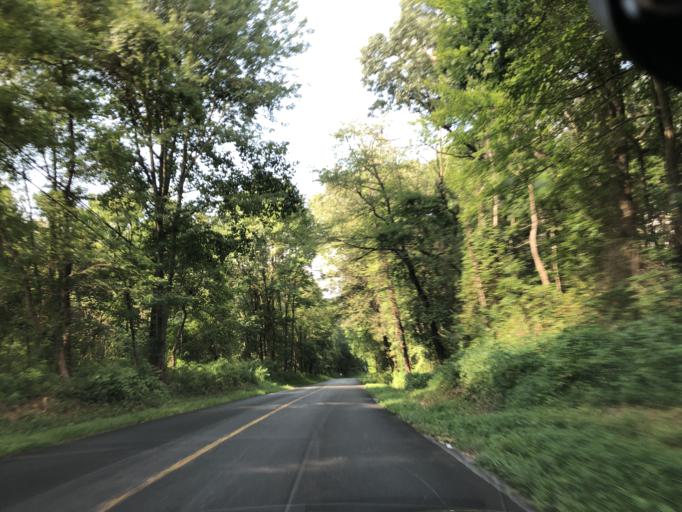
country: US
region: Maryland
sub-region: Carroll County
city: Mount Airy
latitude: 39.4059
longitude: -77.1798
